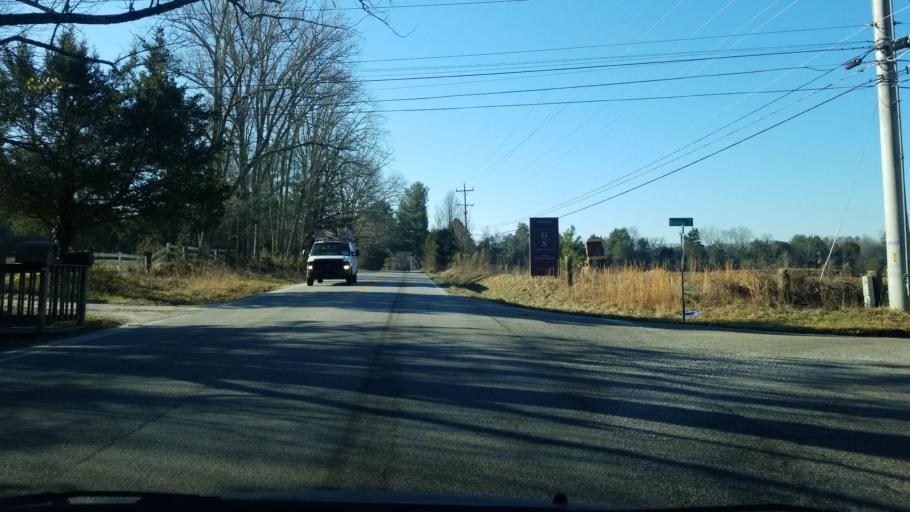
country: US
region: Tennessee
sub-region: Hamilton County
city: Collegedale
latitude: 35.0396
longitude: -85.0761
